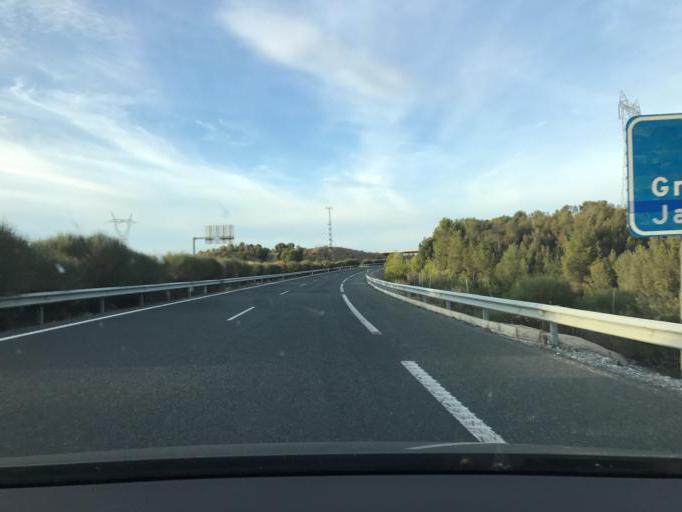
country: ES
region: Andalusia
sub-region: Provincia de Granada
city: Guadix
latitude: 37.2682
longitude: -3.0944
